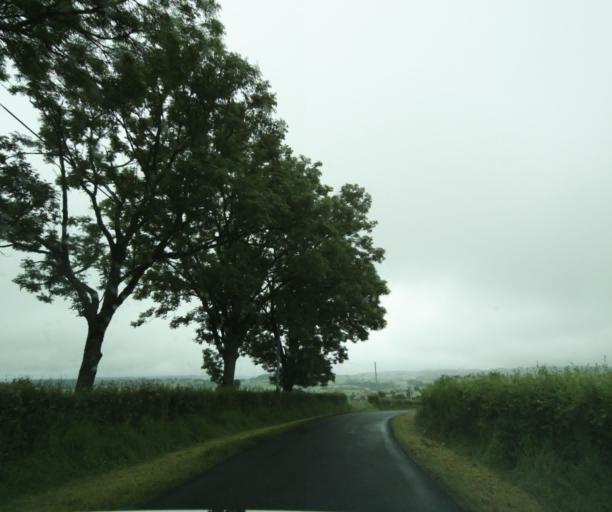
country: FR
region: Bourgogne
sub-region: Departement de Saone-et-Loire
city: Charolles
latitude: 46.3579
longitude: 4.2266
